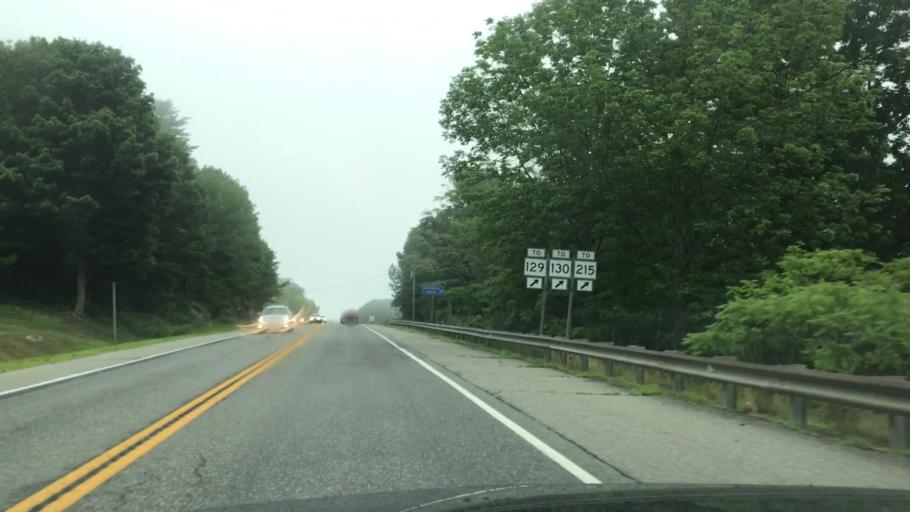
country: US
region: Maine
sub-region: Lincoln County
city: Damariscotta
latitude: 44.0301
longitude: -69.5462
